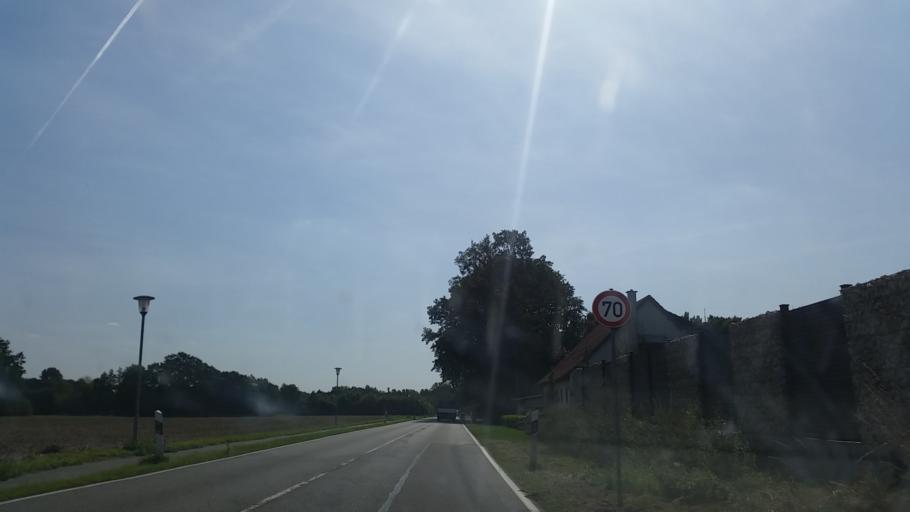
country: DE
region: Lower Saxony
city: Ankum
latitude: 52.5386
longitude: 7.8834
